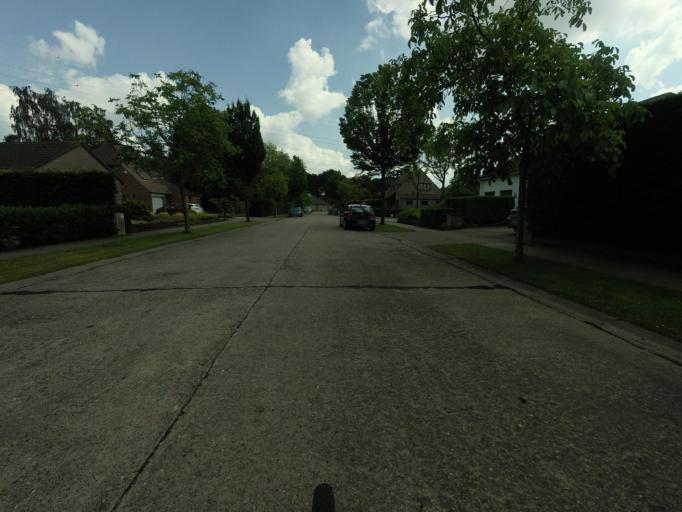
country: BE
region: Flanders
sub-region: Provincie Antwerpen
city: Lint
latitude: 51.1237
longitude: 4.5151
